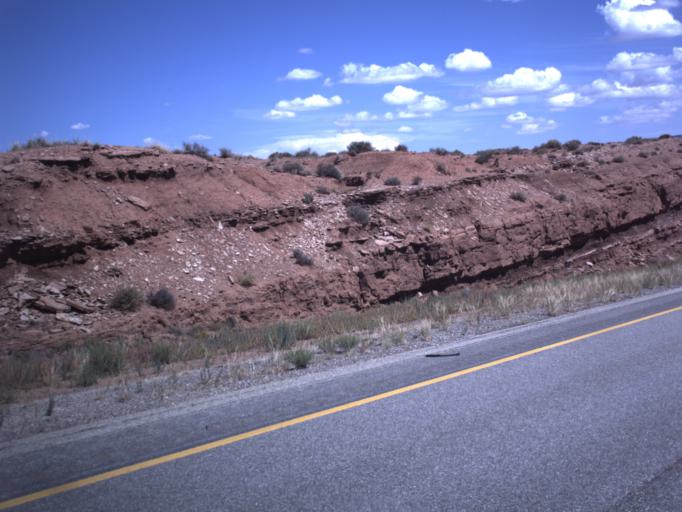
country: US
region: Utah
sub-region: Emery County
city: Ferron
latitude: 38.8393
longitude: -111.0870
